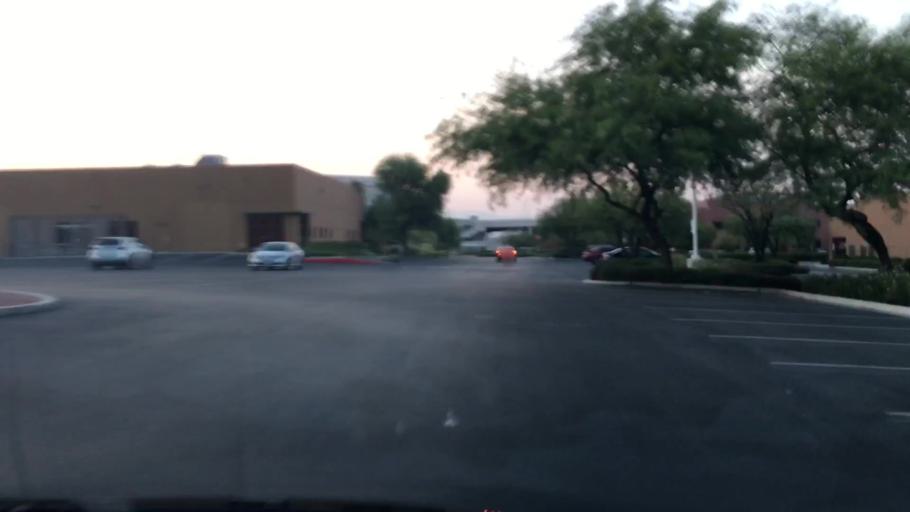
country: US
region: Nevada
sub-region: Clark County
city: Paradise
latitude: 36.0576
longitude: -115.1527
